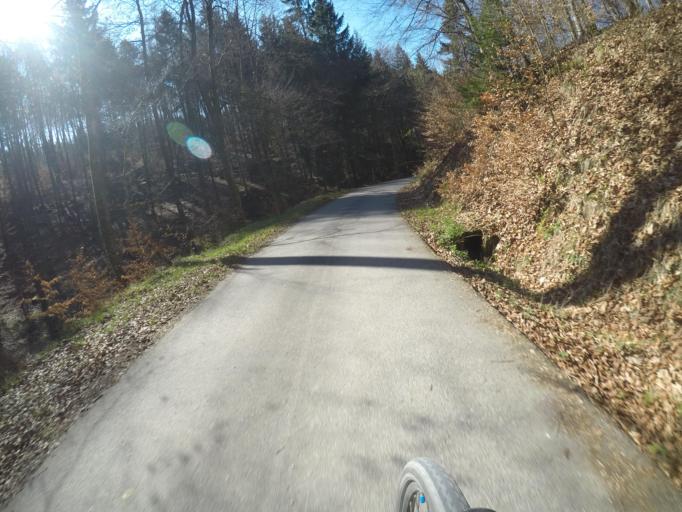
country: DE
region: Baden-Wuerttemberg
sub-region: Tuebingen Region
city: Tuebingen
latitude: 48.5638
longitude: 9.0197
